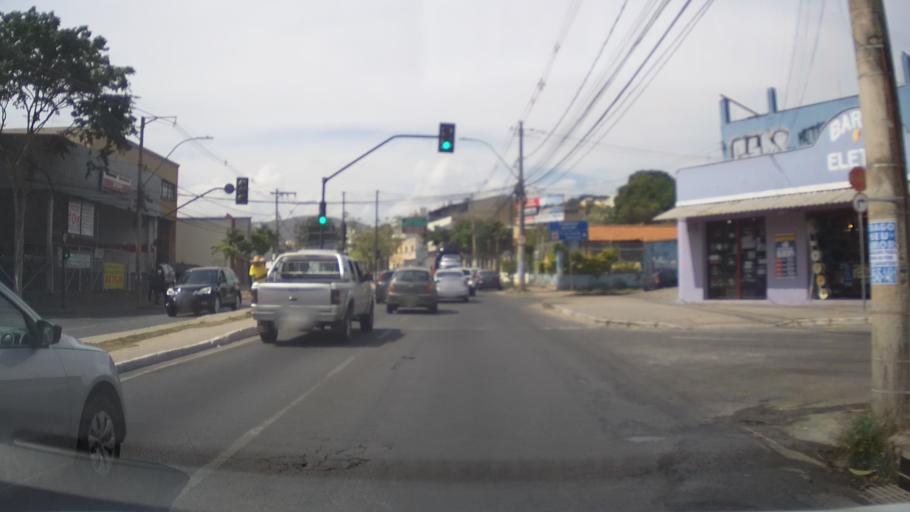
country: BR
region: Minas Gerais
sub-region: Belo Horizonte
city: Belo Horizonte
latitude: -19.9477
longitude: -43.9695
